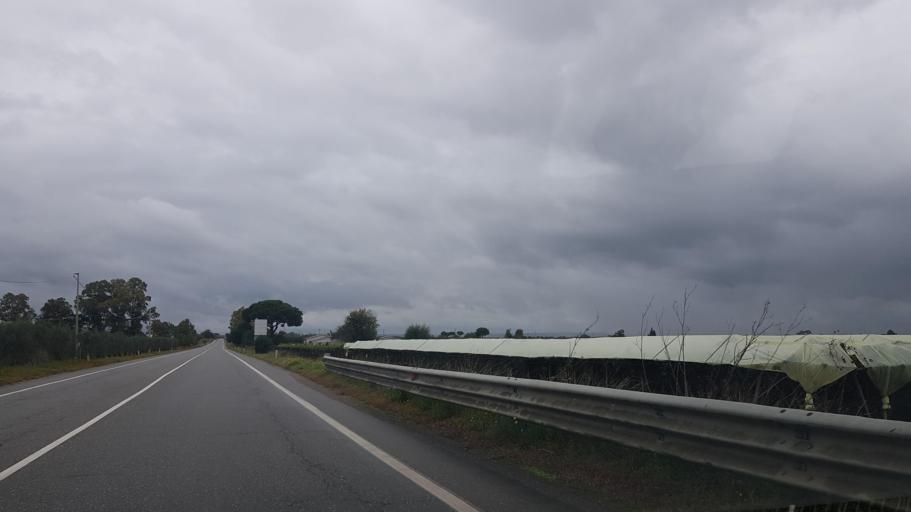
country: IT
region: Apulia
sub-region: Provincia di Taranto
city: Marina di Ginosa
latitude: 40.4067
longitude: 16.8047
